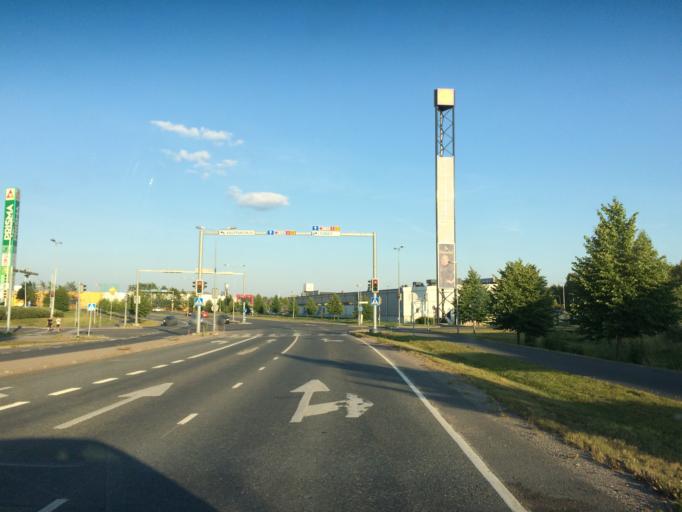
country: FI
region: Haeme
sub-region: Haemeenlinna
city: Haemeenlinna
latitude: 61.0104
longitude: 24.4123
